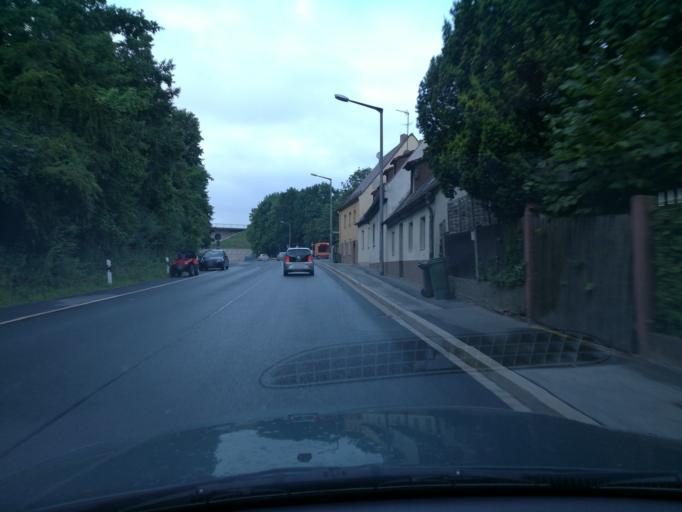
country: DE
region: Bavaria
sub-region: Regierungsbezirk Mittelfranken
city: Obermichelbach
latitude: 49.5298
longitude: 10.9661
